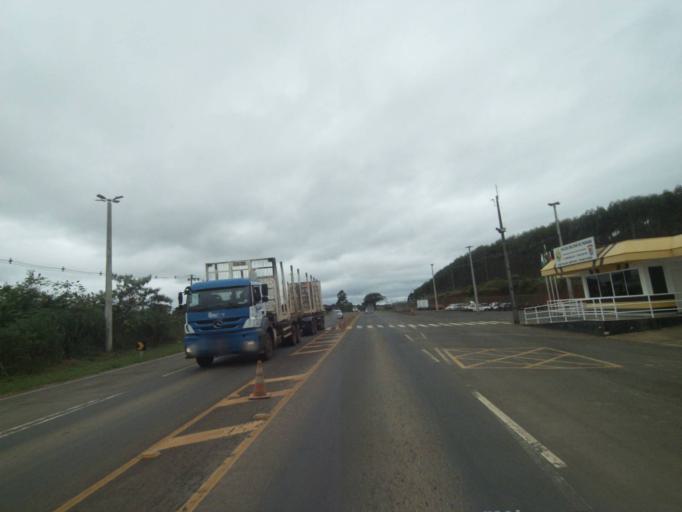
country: BR
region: Parana
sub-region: Telemaco Borba
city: Telemaco Borba
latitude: -24.3865
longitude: -50.6805
